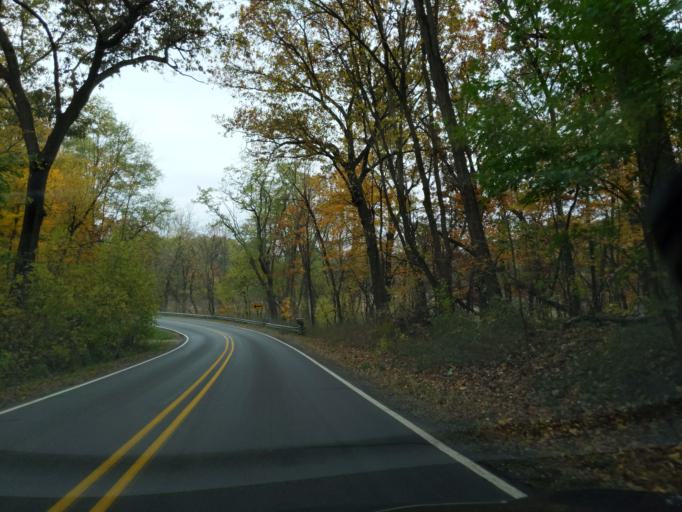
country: US
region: Michigan
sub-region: Jackson County
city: Spring Arbor
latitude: 42.3333
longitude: -84.6006
